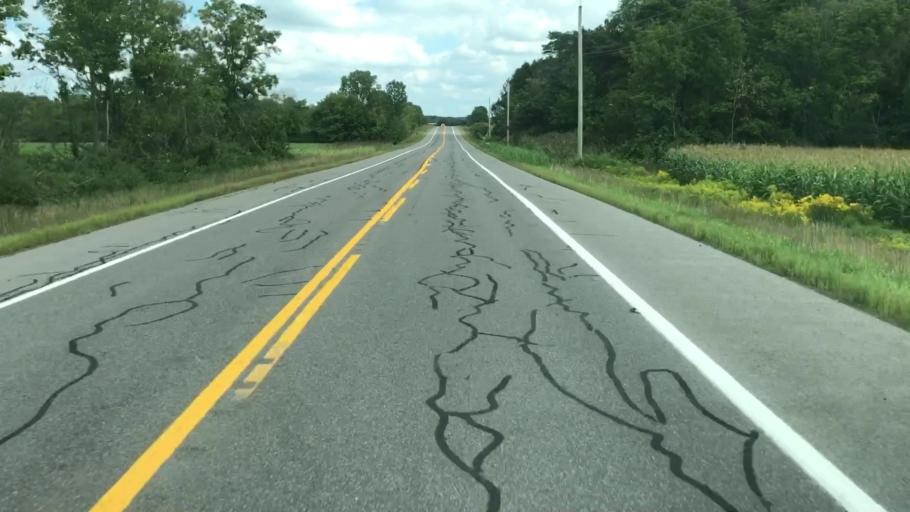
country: US
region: New York
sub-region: Onondaga County
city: Skaneateles
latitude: 42.9463
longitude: -76.3852
